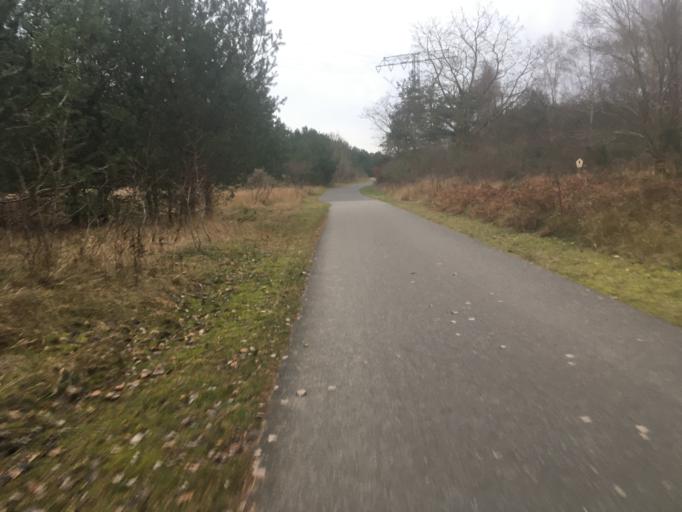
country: DE
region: Mecklenburg-Vorpommern
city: Sagard
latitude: 54.4608
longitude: 13.5665
